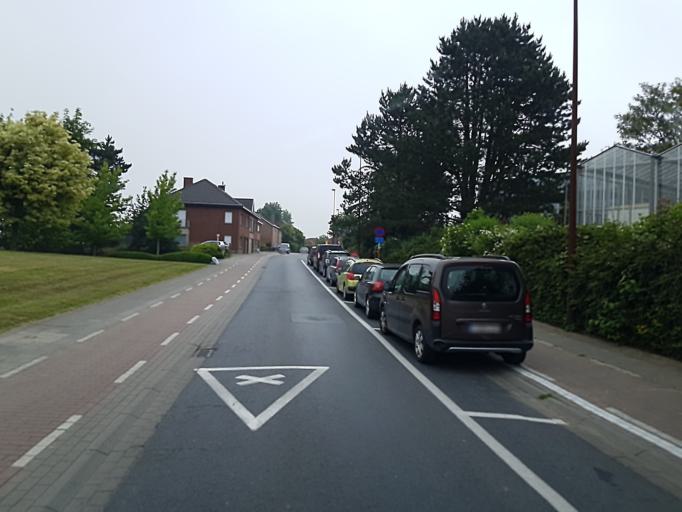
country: BE
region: Flanders
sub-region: Provincie West-Vlaanderen
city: Moorslede
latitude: 50.8950
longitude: 3.0585
